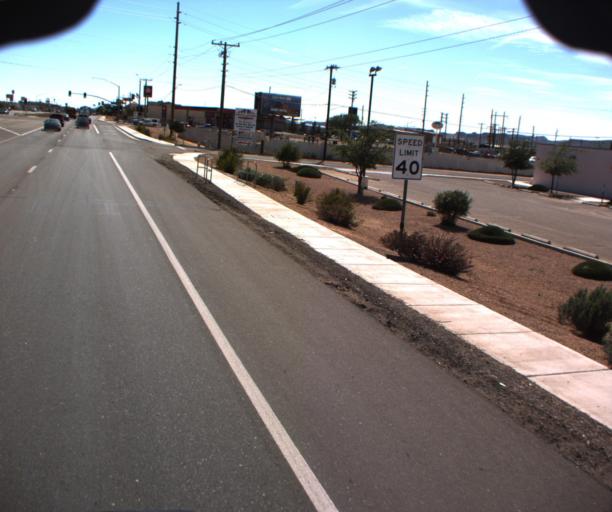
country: US
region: Arizona
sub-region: Mohave County
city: New Kingman-Butler
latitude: 35.2256
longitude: -114.0028
